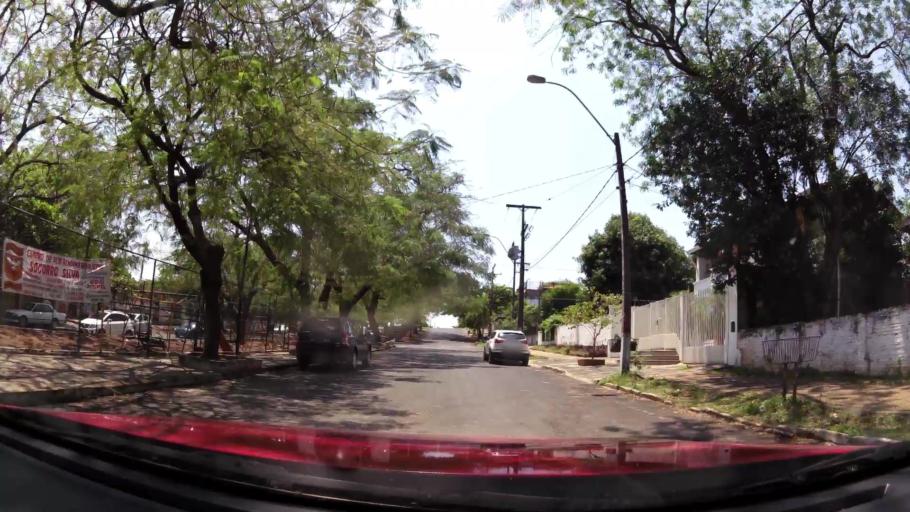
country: PY
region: Asuncion
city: Asuncion
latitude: -25.3061
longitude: -57.6393
